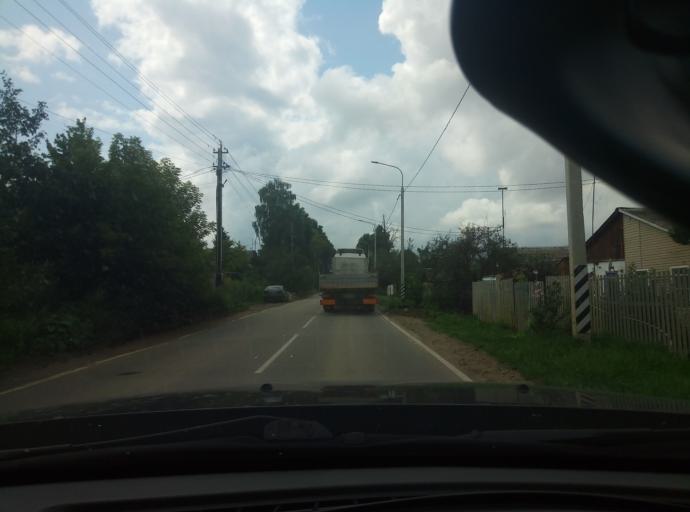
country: RU
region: Tula
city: Borodinskiy
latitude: 53.9987
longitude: 37.8134
